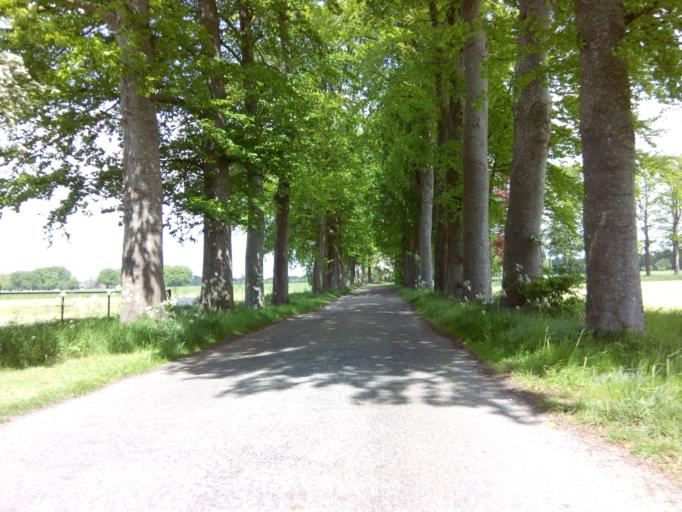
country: NL
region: Utrecht
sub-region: Gemeente Utrechtse Heuvelrug
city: Overberg
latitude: 52.0623
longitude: 5.4702
